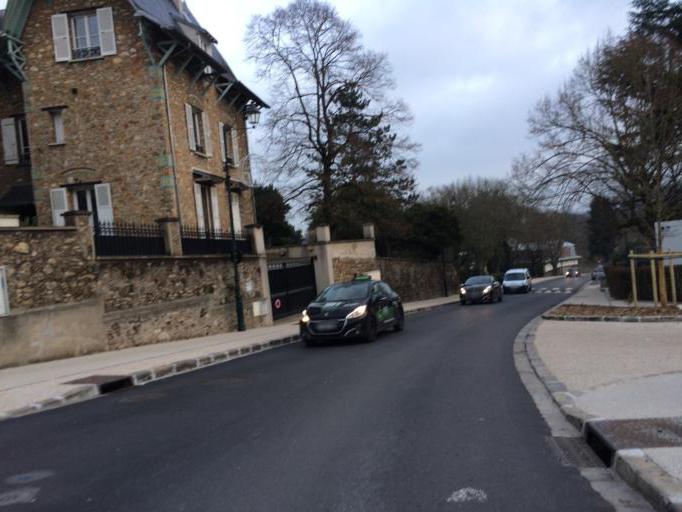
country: FR
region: Ile-de-France
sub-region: Departement de l'Essonne
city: Bievres
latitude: 48.7548
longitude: 2.2152
